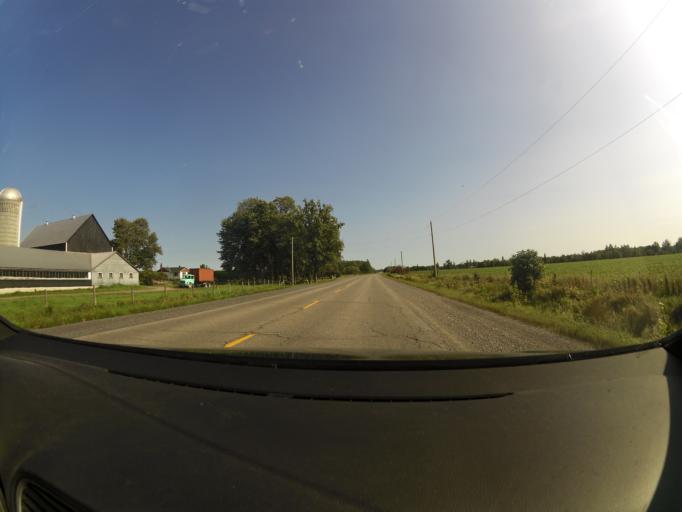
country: CA
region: Ontario
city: Arnprior
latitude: 45.3786
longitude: -76.3154
